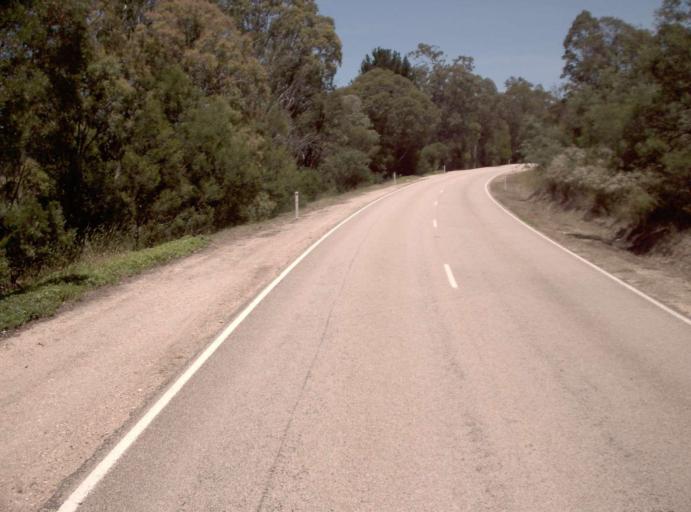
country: AU
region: Victoria
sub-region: East Gippsland
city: Lakes Entrance
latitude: -37.6704
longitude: 147.8683
